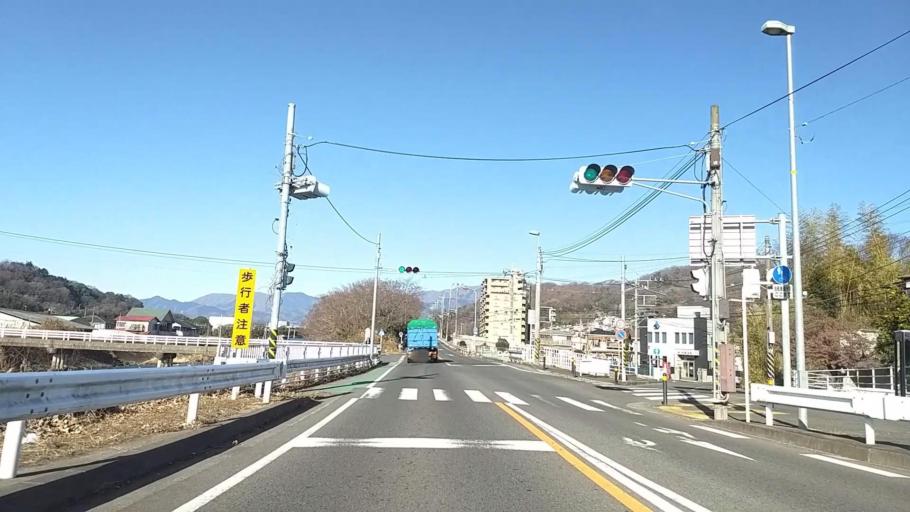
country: JP
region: Kanagawa
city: Hadano
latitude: 35.3610
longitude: 139.2494
